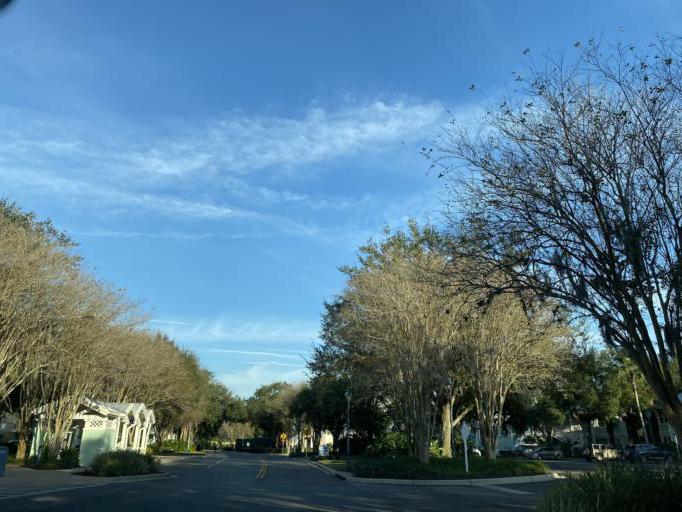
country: US
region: Florida
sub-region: Osceola County
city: Celebration
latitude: 28.3718
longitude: -81.5337
